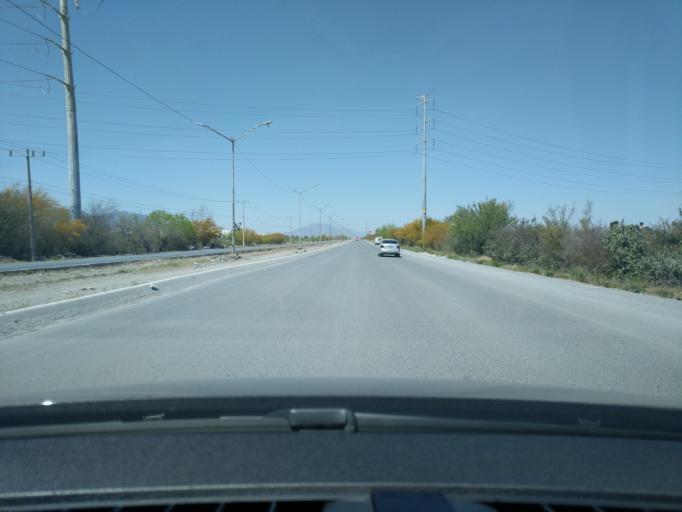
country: MX
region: Nuevo Leon
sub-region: Salinas Victoria
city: Emiliano Zapata
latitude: 25.9185
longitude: -100.2700
